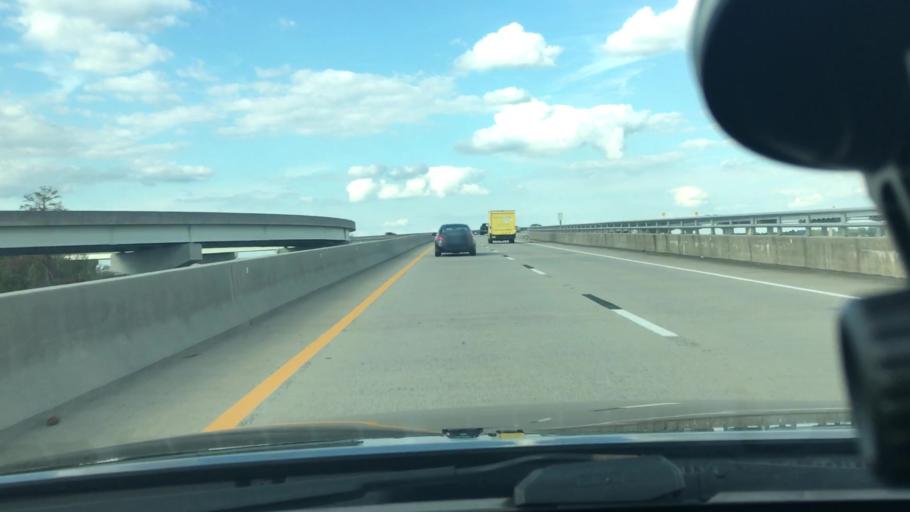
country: US
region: North Carolina
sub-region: Craven County
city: James City
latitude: 35.0923
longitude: -77.0350
